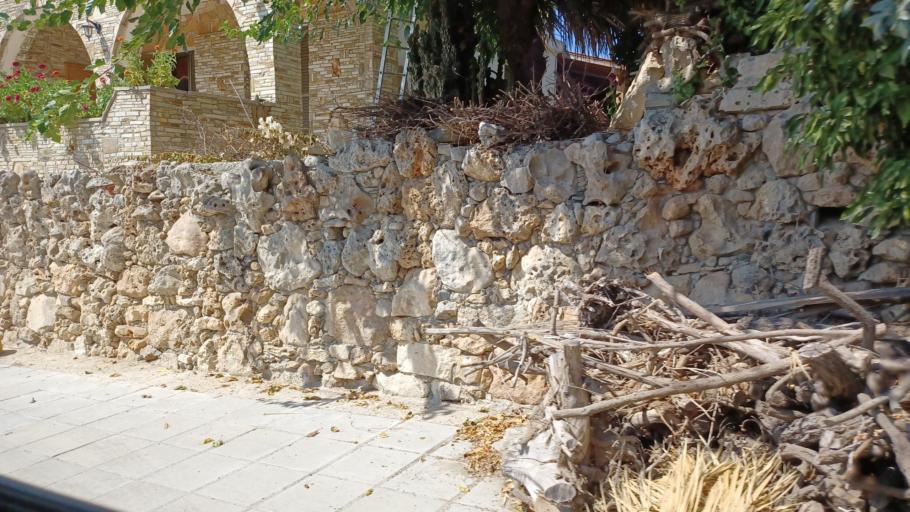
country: CY
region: Pafos
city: Tala
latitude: 34.9232
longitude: 32.4764
